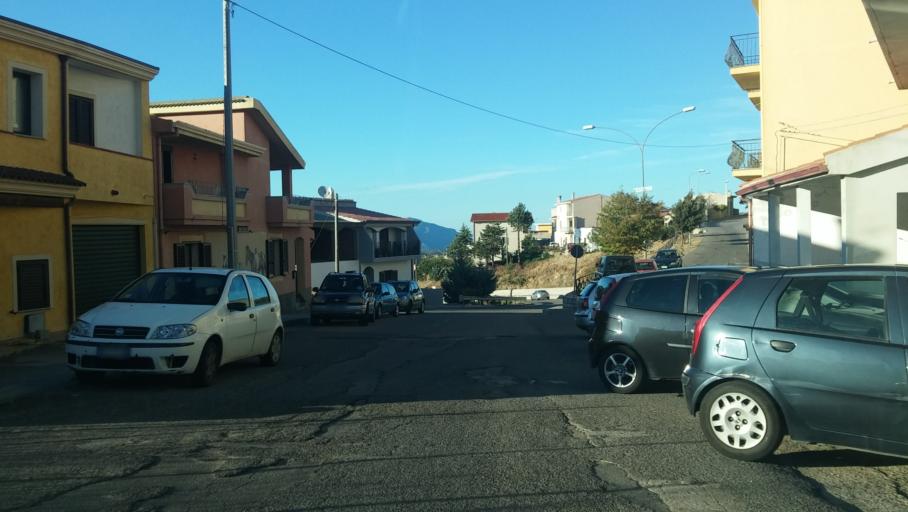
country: IT
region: Sardinia
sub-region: Provincia di Nuoro
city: Orgosolo
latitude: 40.2041
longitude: 9.3482
